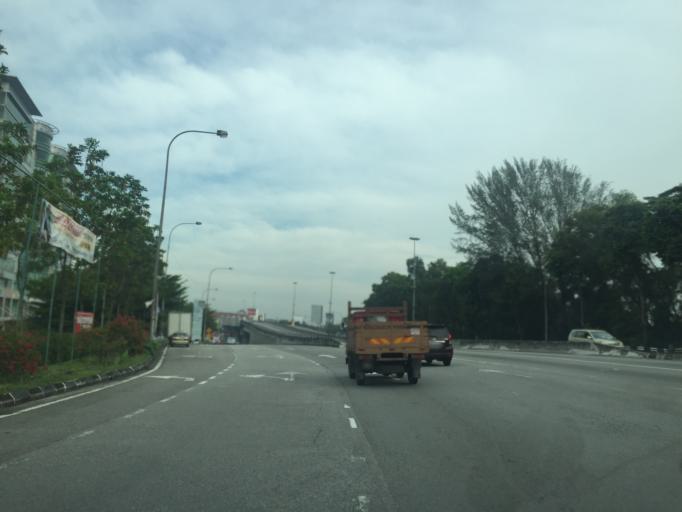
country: MY
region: Selangor
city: Klang
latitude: 3.0068
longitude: 101.4420
